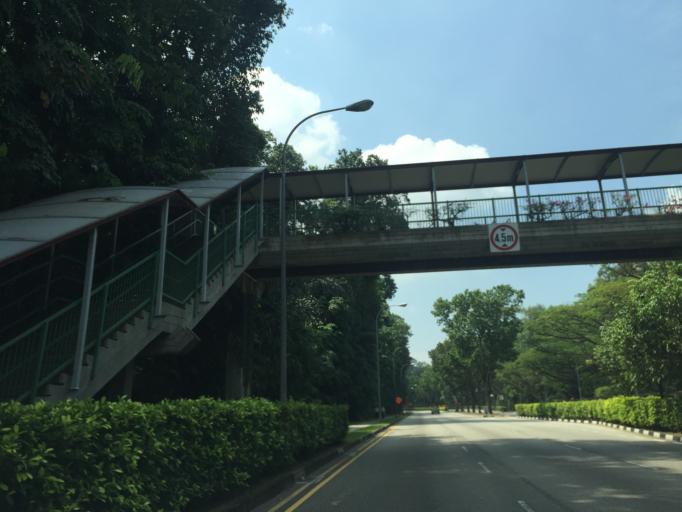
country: SG
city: Singapore
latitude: 1.3078
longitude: 103.8108
